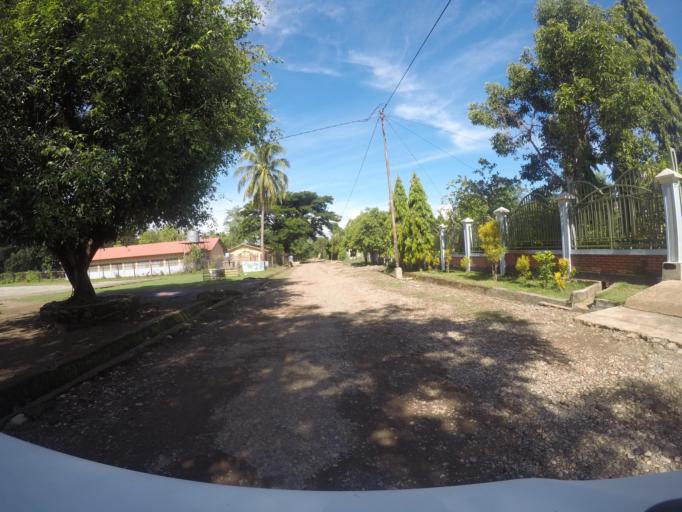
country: TL
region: Bobonaro
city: Maliana
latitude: -8.9877
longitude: 125.2021
